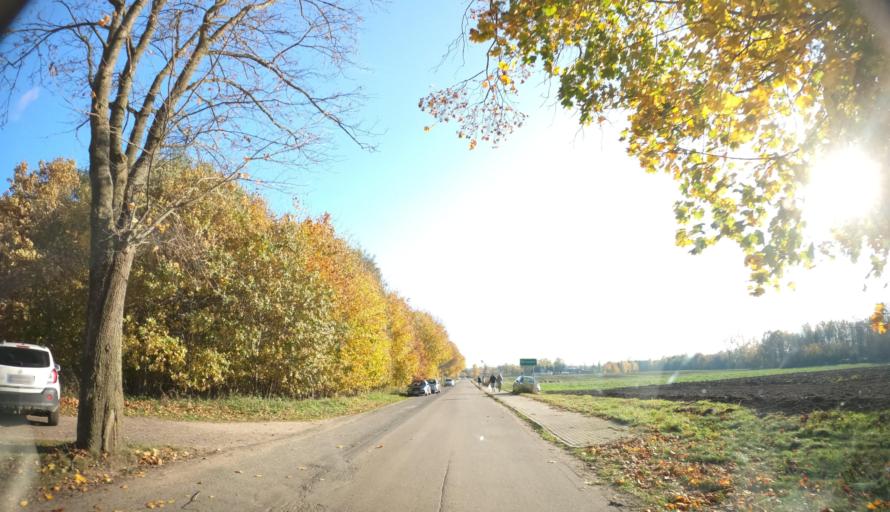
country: PL
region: West Pomeranian Voivodeship
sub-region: Powiat slawienski
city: Slawno
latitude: 54.2828
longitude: 16.6663
